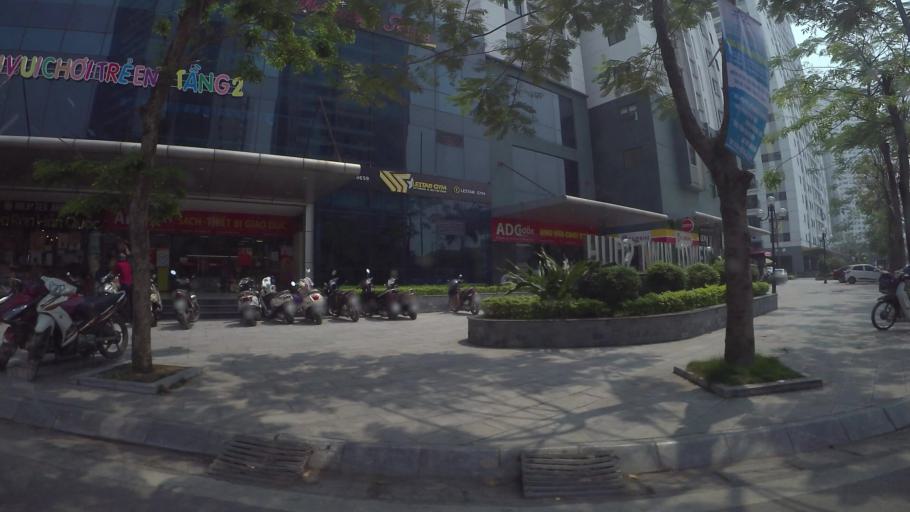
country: VN
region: Ha Noi
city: Van Dien
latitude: 20.9638
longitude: 105.8230
